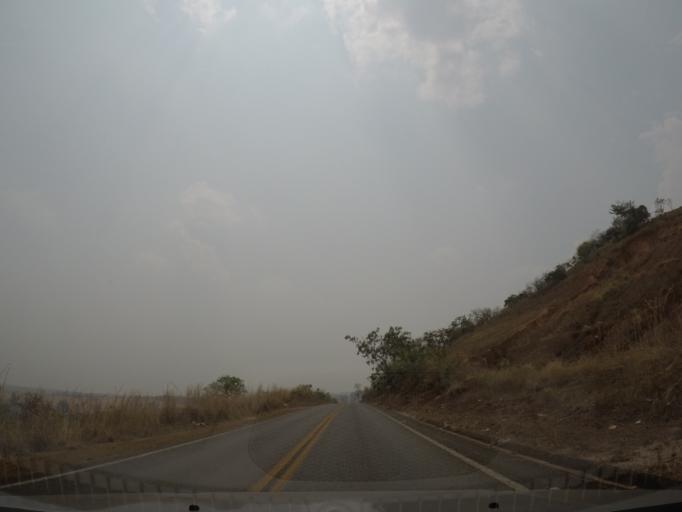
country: BR
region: Goias
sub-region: Pirenopolis
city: Pirenopolis
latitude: -15.9263
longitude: -48.8518
